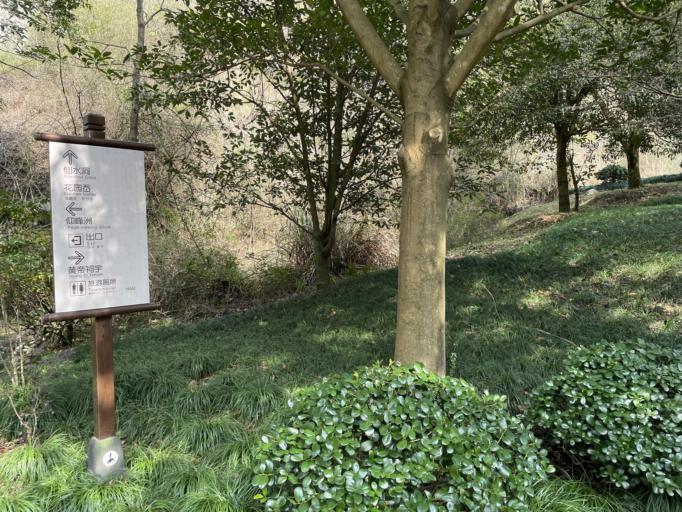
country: CN
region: Zhejiang Sheng
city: Shuhong
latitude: 28.6916
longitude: 120.1386
